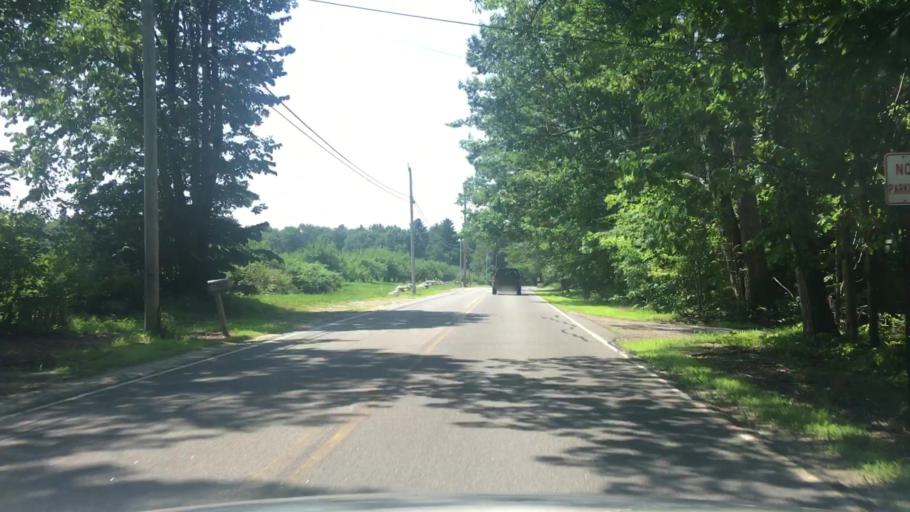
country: US
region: Maine
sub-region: Cumberland County
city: Cumberland Center
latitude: 43.8302
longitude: -70.2986
